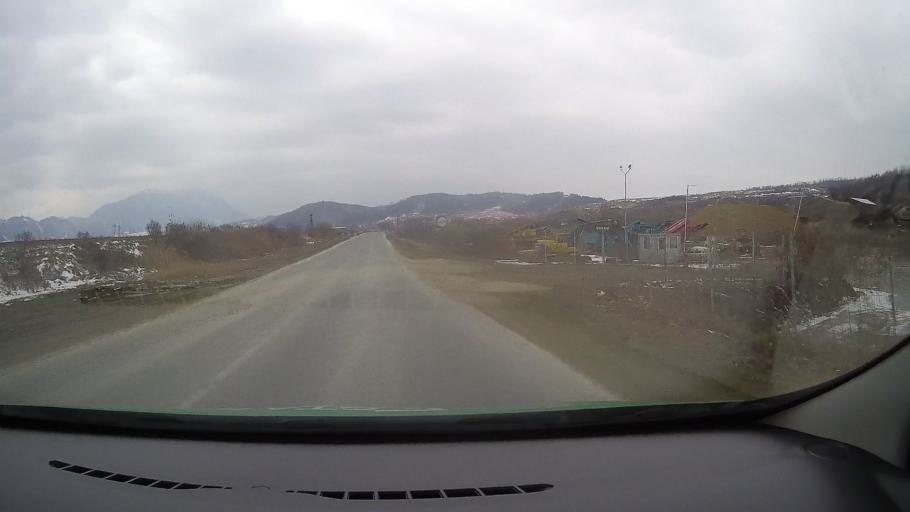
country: RO
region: Brasov
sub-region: Comuna Zarnesti
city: Tohanu Nou
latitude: 45.5771
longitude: 25.3940
